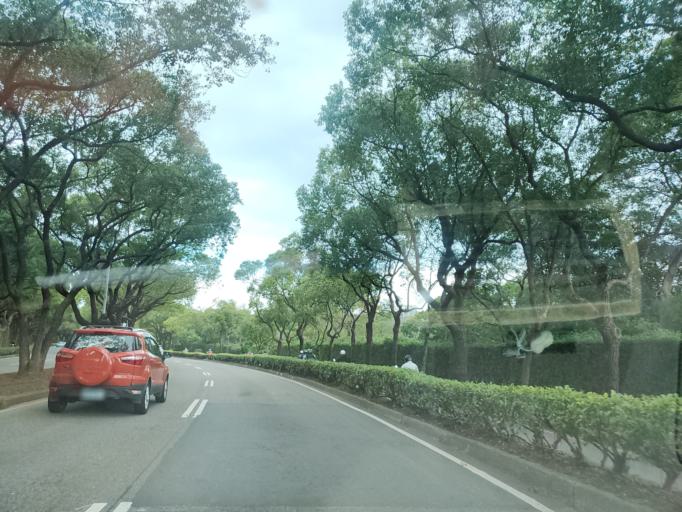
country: TW
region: Taiwan
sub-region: Hsinchu
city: Hsinchu
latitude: 24.7815
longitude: 121.0069
